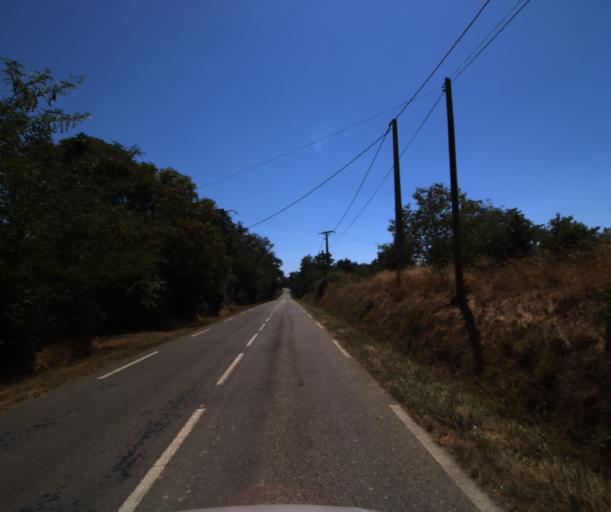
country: FR
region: Midi-Pyrenees
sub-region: Departement de la Haute-Garonne
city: Seysses
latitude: 43.4573
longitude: 1.2930
